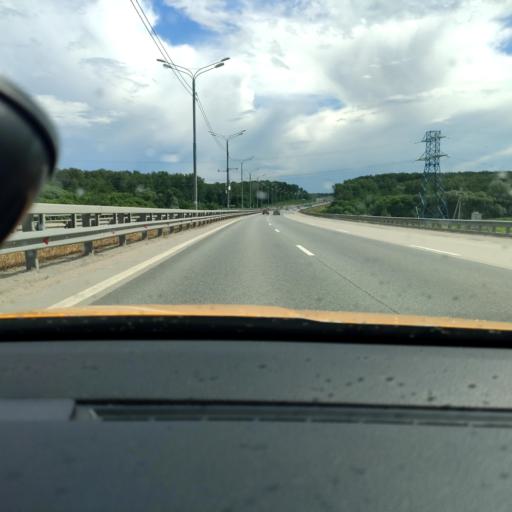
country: RU
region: Moskovskaya
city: Barybino
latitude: 55.2761
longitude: 37.8653
